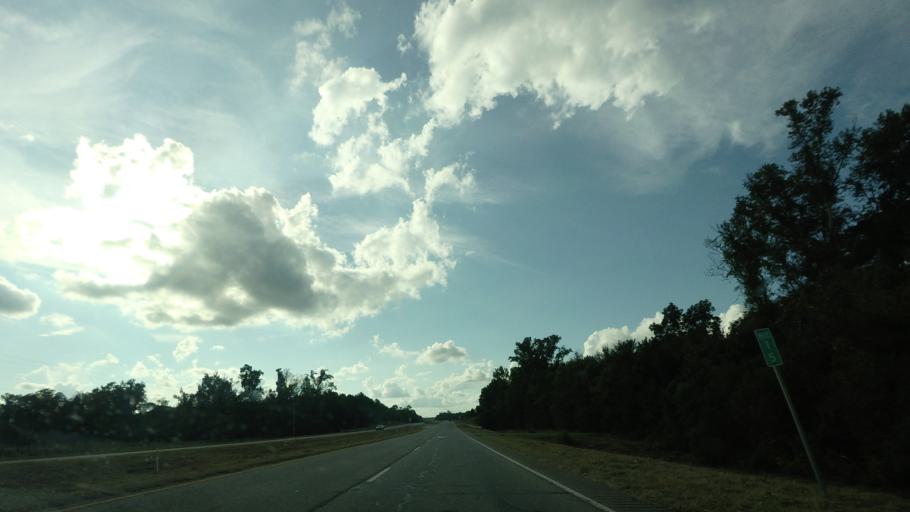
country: US
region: Georgia
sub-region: Pulaski County
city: Hawkinsville
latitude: 32.3110
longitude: -83.5154
